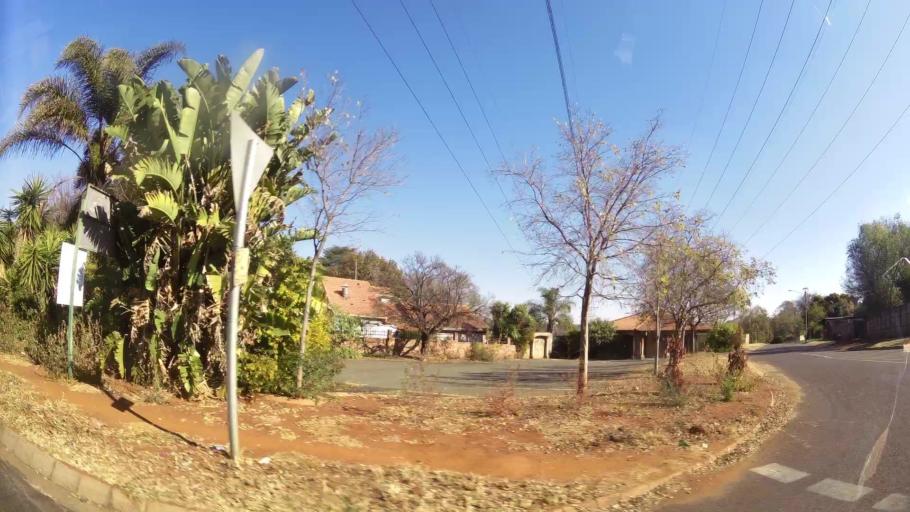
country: ZA
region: Gauteng
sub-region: City of Tshwane Metropolitan Municipality
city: Centurion
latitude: -25.8232
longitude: 28.1630
